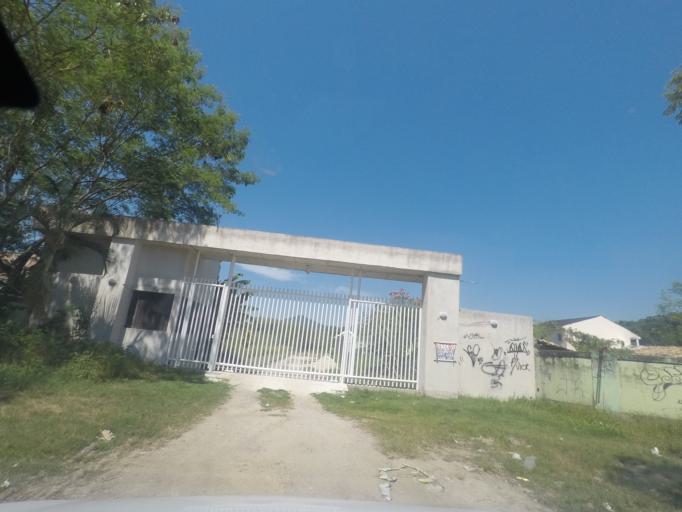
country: BR
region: Rio de Janeiro
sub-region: Nilopolis
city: Nilopolis
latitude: -22.9896
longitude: -43.4762
